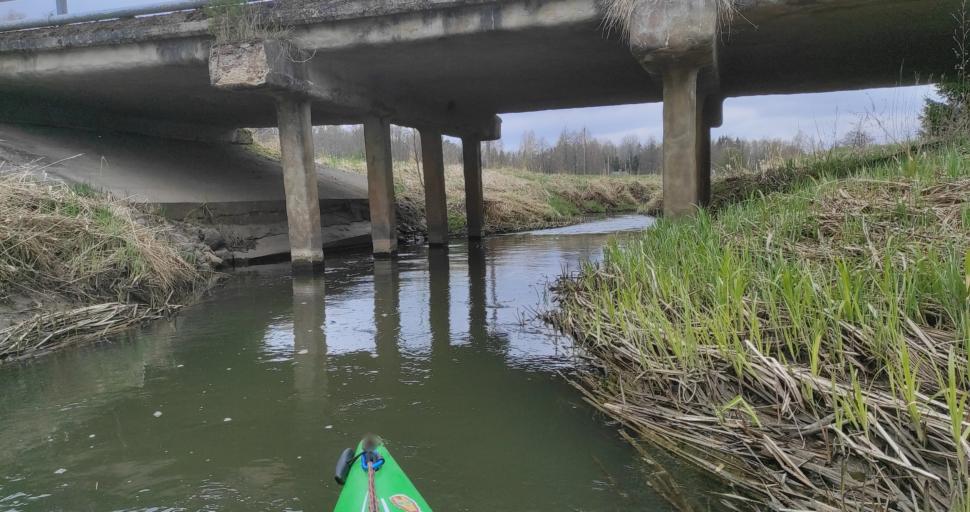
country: LV
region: Alsunga
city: Alsunga
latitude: 56.8386
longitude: 21.4957
